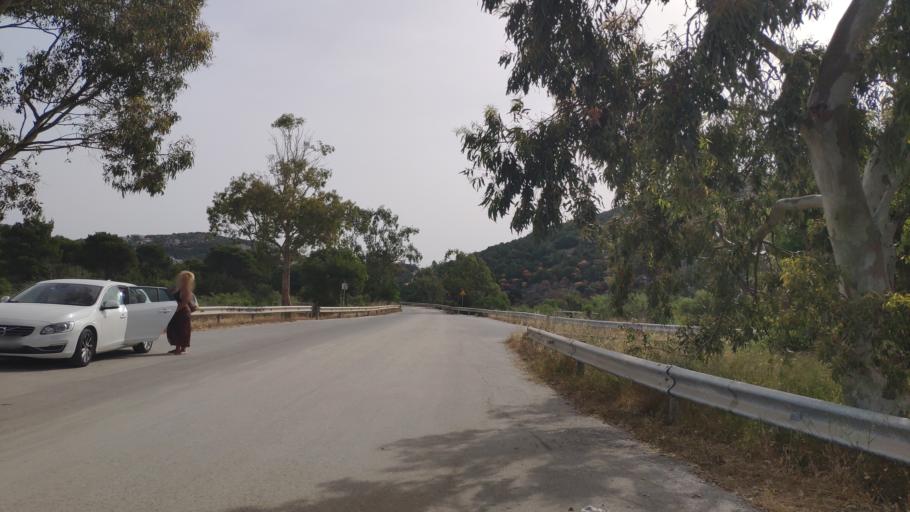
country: GR
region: Attica
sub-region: Nomarchia Anatolikis Attikis
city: Kato Soulion
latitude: 38.1433
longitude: 24.0510
